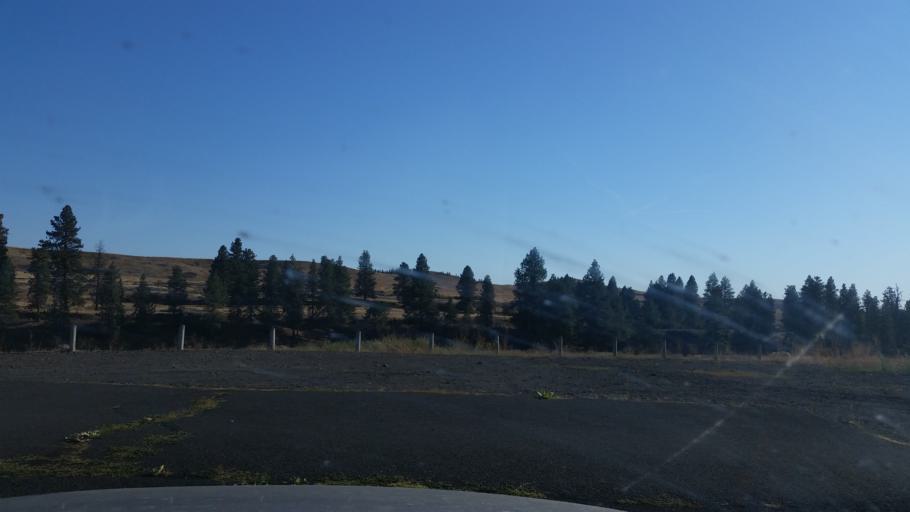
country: US
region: Washington
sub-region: Spokane County
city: Cheney
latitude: 47.3486
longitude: -117.7151
